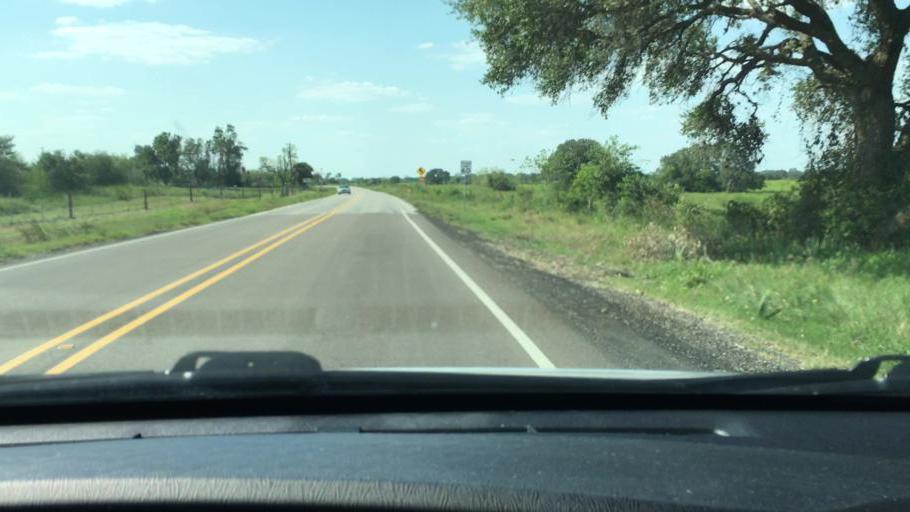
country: US
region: Texas
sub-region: DeWitt County
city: Yorktown
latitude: 28.9205
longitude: -97.3475
